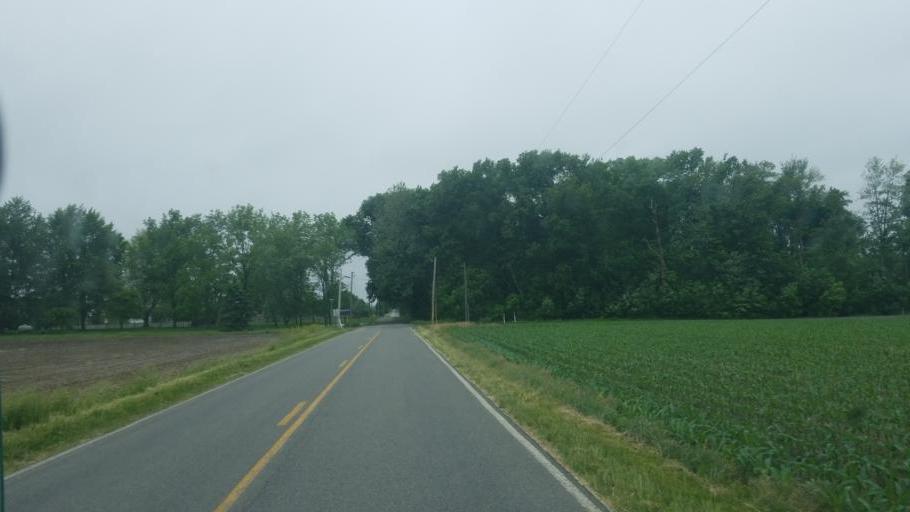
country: US
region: Indiana
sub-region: Marshall County
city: Bremen
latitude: 41.4799
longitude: -86.1178
